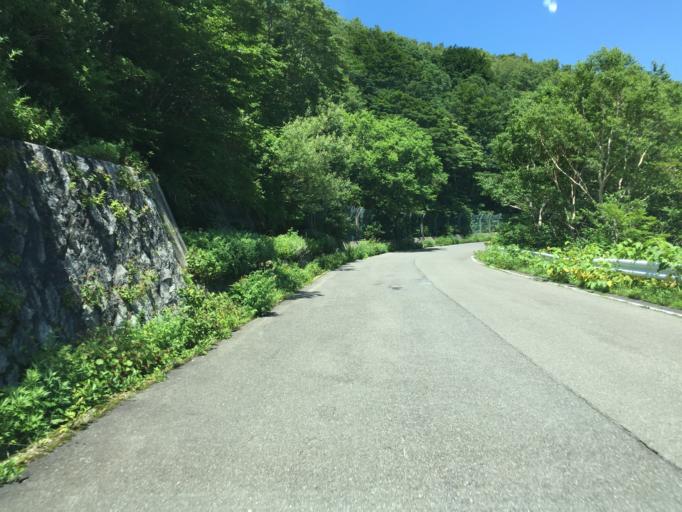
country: JP
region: Fukushima
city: Nihommatsu
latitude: 37.6649
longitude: 140.2803
